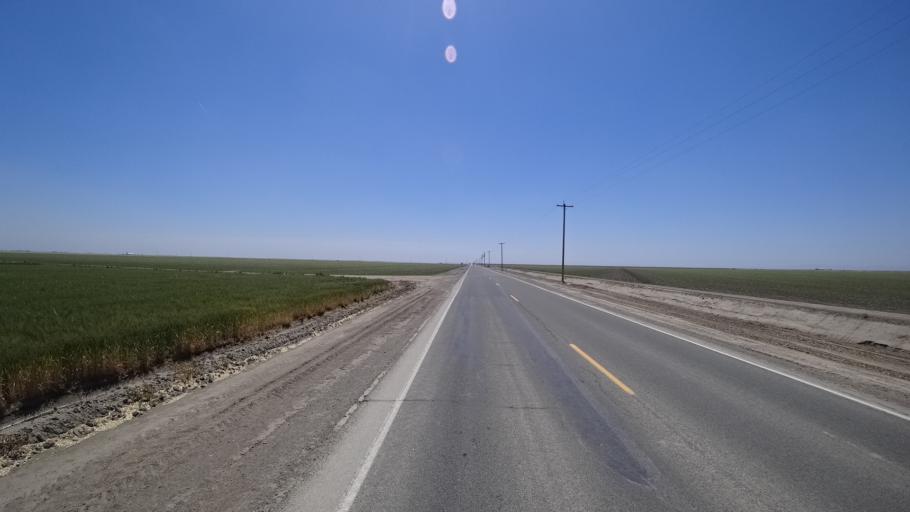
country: US
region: California
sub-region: Kings County
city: Corcoran
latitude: 36.1056
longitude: -119.6443
